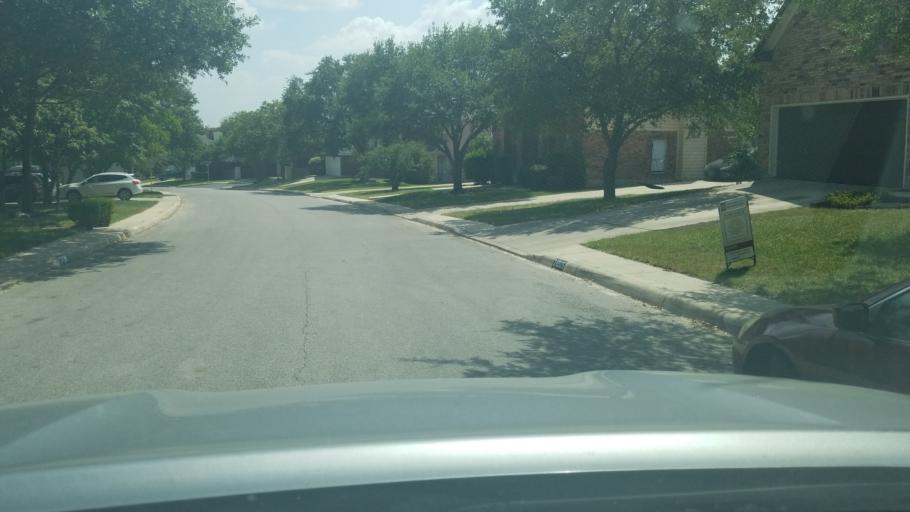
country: US
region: Texas
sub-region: Bexar County
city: Hollywood Park
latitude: 29.6410
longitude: -98.4998
